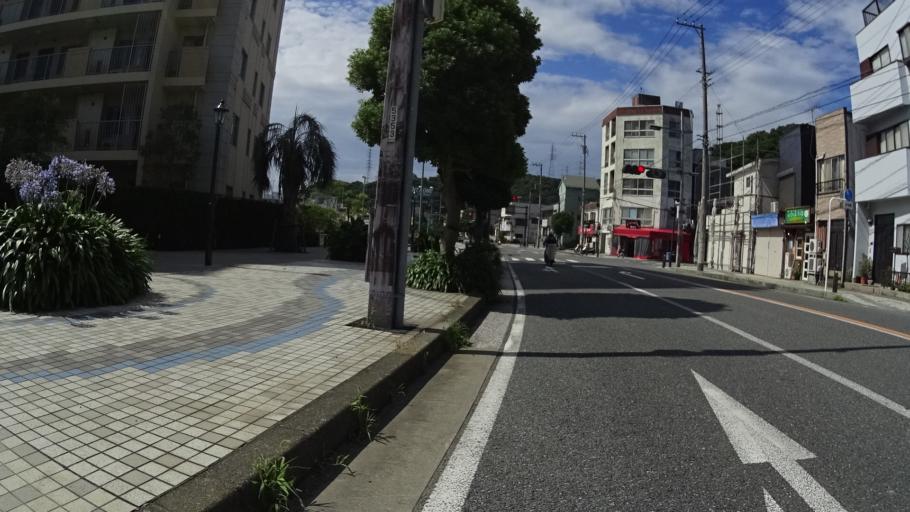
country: JP
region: Kanagawa
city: Yokosuka
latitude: 35.2231
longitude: 139.7121
